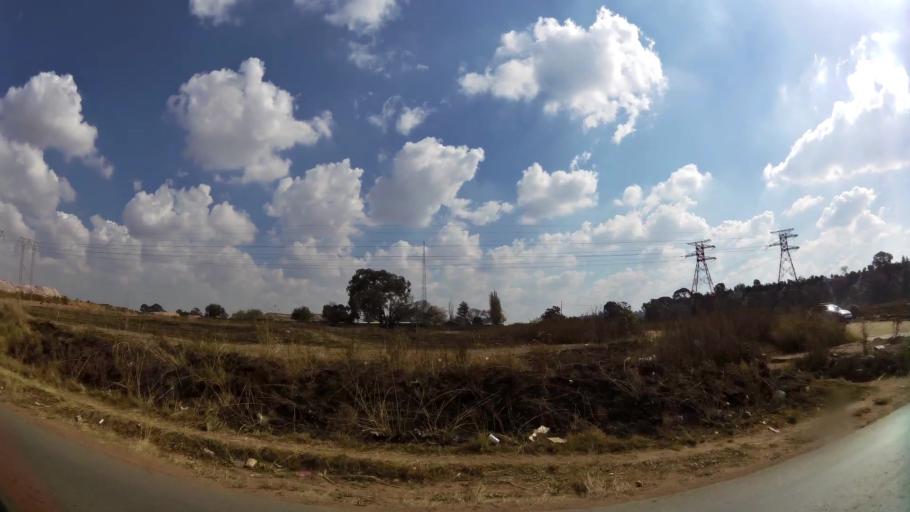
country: ZA
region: Gauteng
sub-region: City of Johannesburg Metropolitan Municipality
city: Roodepoort
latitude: -26.1836
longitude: 27.8692
